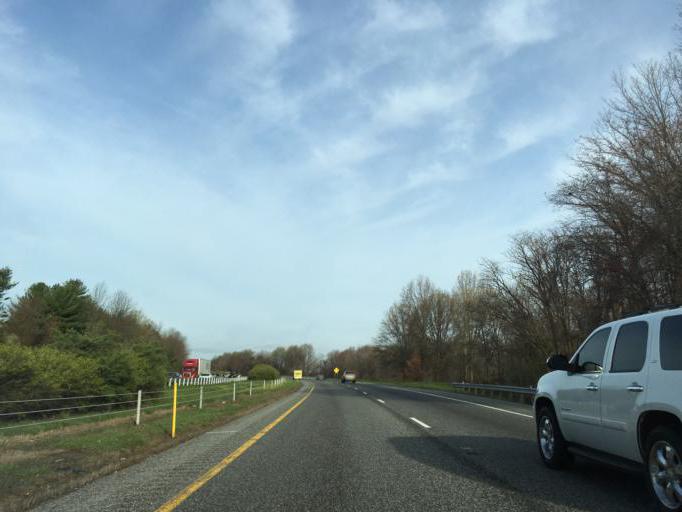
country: US
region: Maryland
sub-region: Carroll County
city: Sykesville
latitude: 39.3039
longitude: -76.9141
